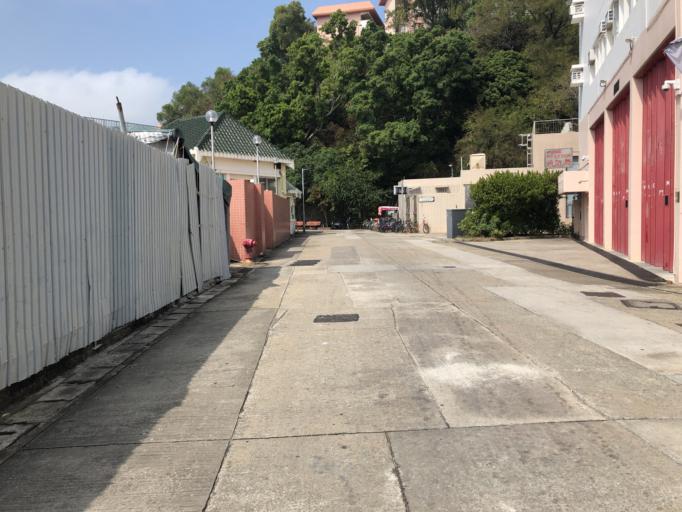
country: HK
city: Yung Shue Wan
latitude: 22.2120
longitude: 114.0263
